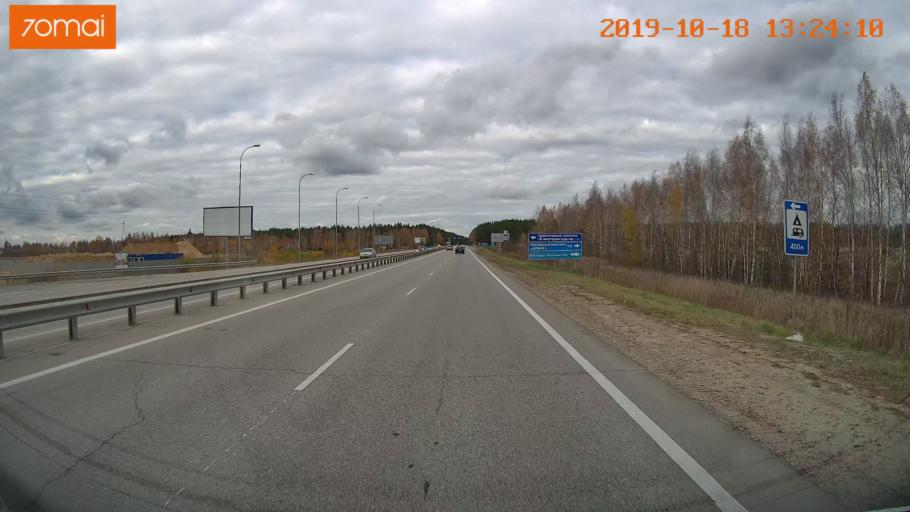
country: RU
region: Rjazan
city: Polyany
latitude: 54.7268
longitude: 39.8456
